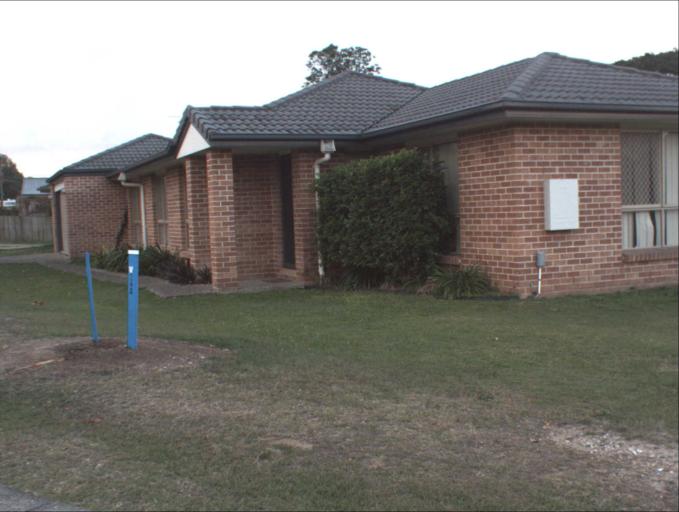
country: AU
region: Queensland
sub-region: Logan
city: Waterford West
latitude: -27.6776
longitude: 153.1318
